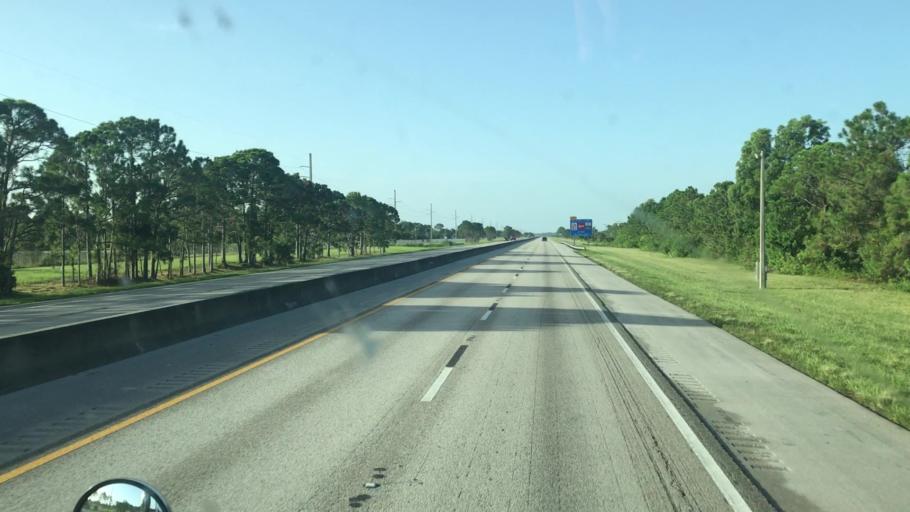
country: US
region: Florida
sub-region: Saint Lucie County
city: River Park
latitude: 27.3402
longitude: -80.3744
